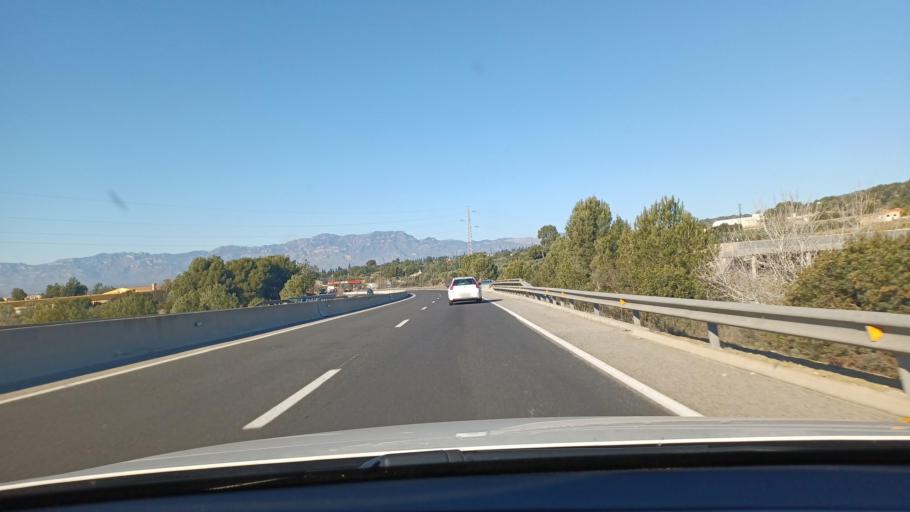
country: ES
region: Catalonia
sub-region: Provincia de Tarragona
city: Amposta
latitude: 40.7637
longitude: 0.5744
